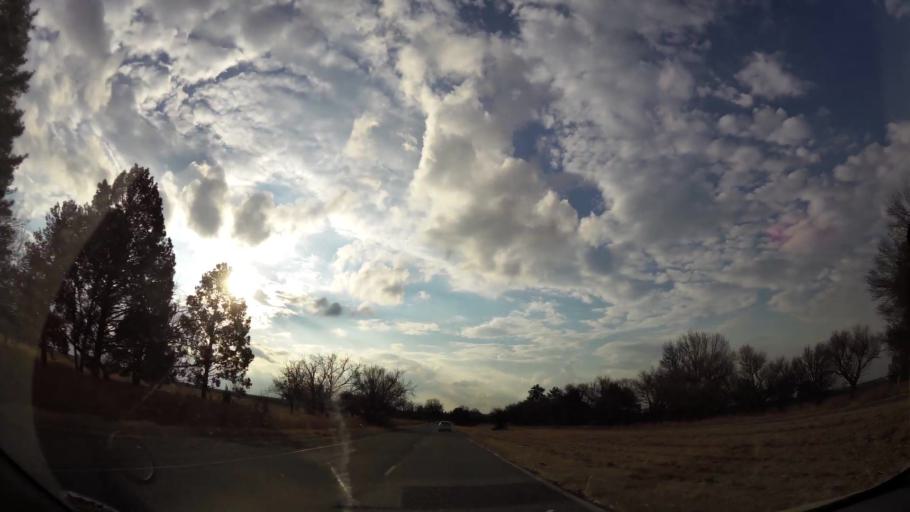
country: ZA
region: Orange Free State
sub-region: Fezile Dabi District Municipality
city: Sasolburg
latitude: -26.7880
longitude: 27.8253
